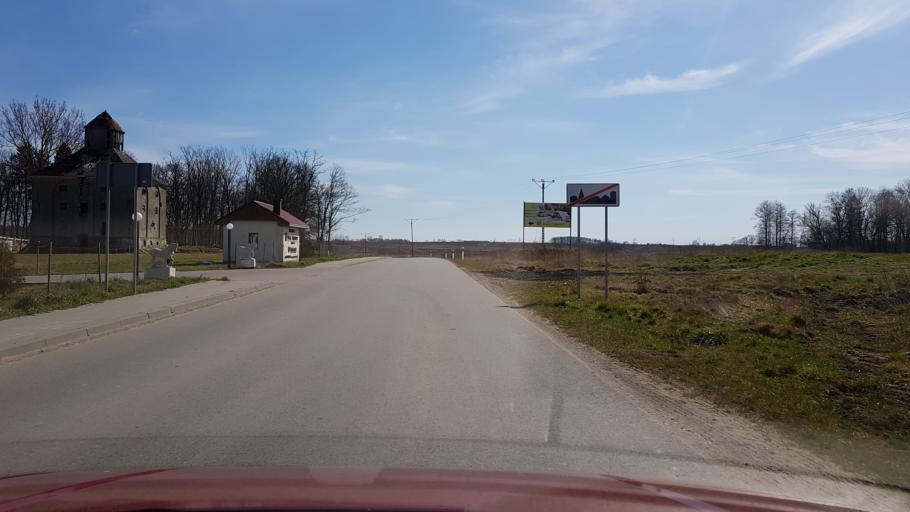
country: PL
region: West Pomeranian Voivodeship
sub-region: Powiat koszalinski
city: Mielno
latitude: 54.1613
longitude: 16.0394
